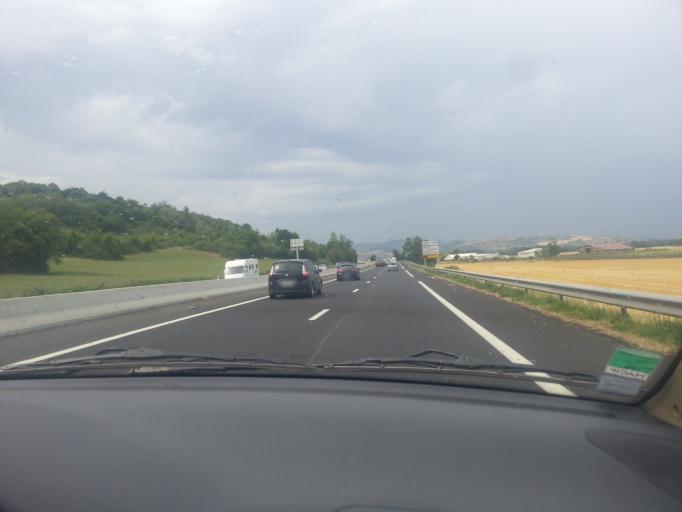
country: FR
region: Auvergne
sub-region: Departement du Puy-de-Dome
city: Le Breuil-sur-Couze
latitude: 45.5058
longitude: 3.2620
